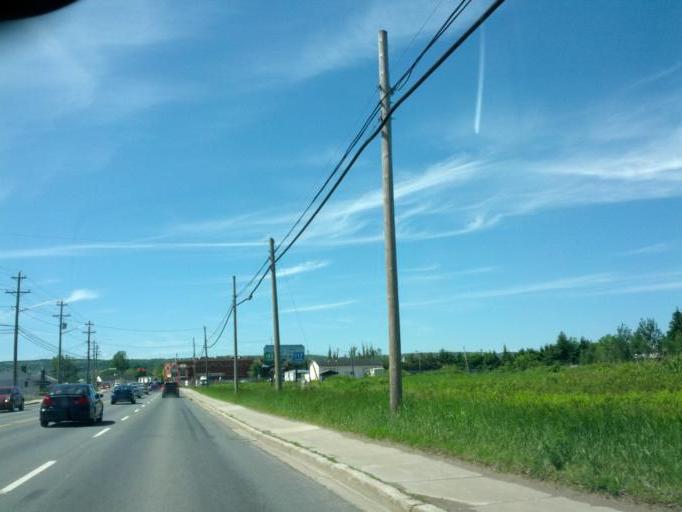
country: CA
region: New Brunswick
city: Moncton
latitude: 46.1195
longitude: -64.8435
